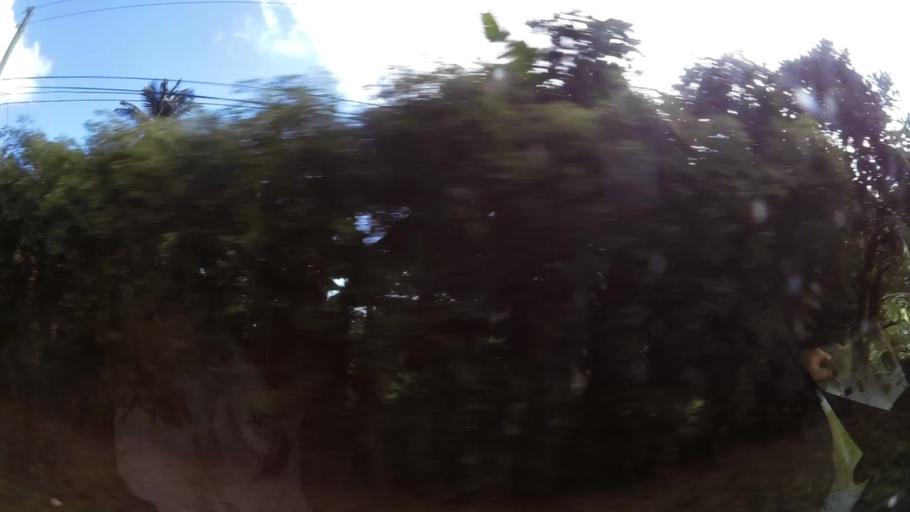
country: DM
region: Saint Andrew
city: Marigot
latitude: 15.4972
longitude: -61.2643
